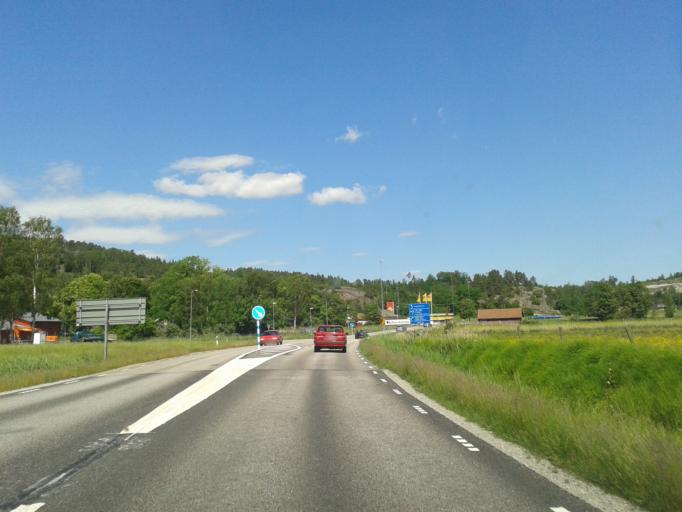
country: SE
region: Vaestra Goetaland
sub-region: Orust
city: Henan
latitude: 58.3398
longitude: 11.6917
